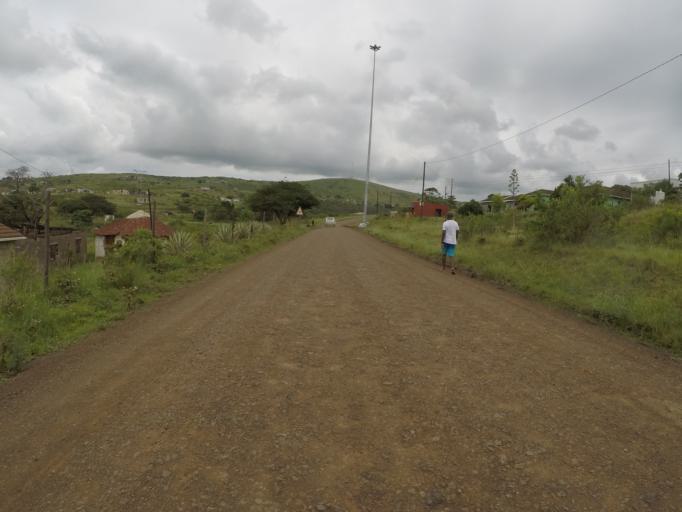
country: ZA
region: KwaZulu-Natal
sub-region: uThungulu District Municipality
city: Empangeni
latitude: -28.7104
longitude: 31.8501
